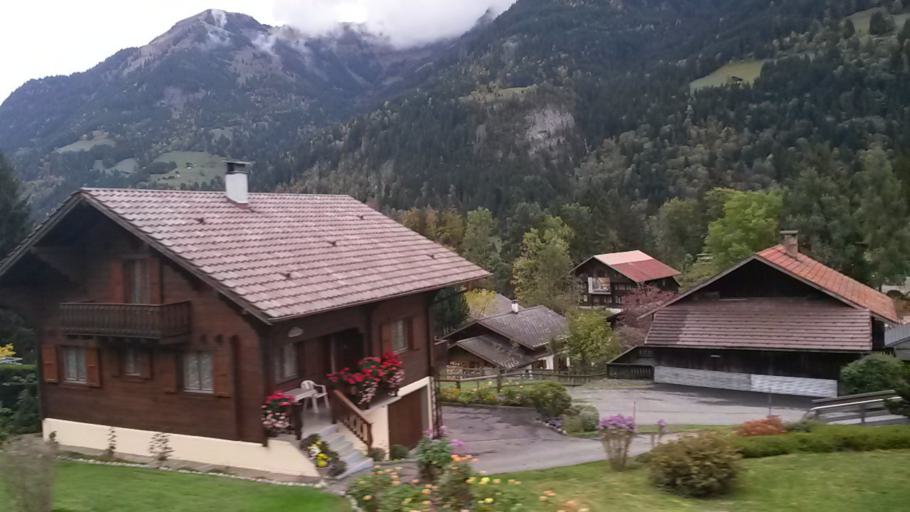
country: CH
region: Valais
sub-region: Monthey District
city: Champery
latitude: 46.1787
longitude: 6.8718
